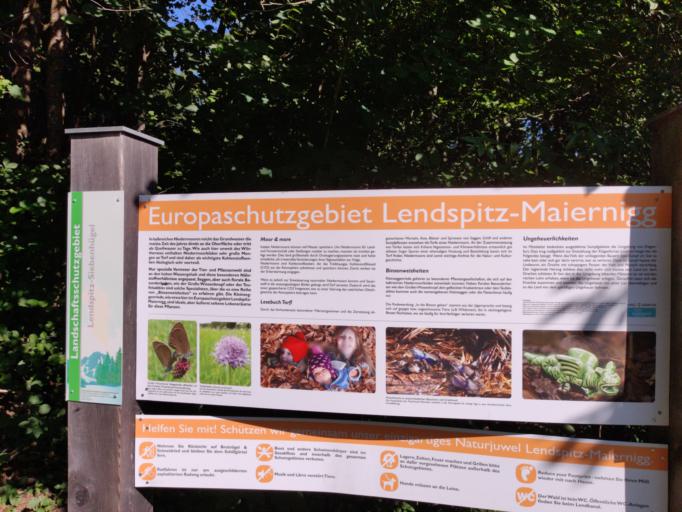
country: AT
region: Carinthia
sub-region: Klagenfurt am Woerthersee
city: Klagenfurt am Woerthersee
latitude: 46.6131
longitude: 14.2572
